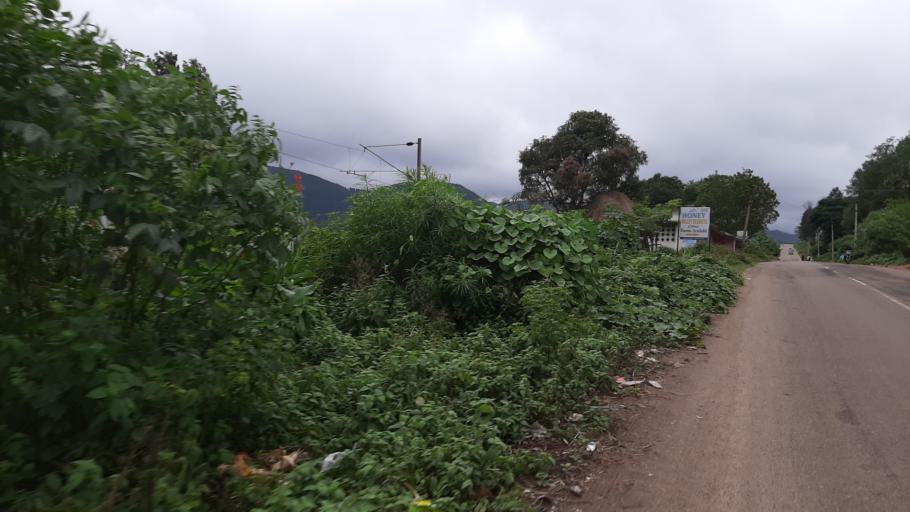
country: IN
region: Andhra Pradesh
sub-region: Vizianagaram District
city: Salur
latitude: 18.3052
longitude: 82.9049
